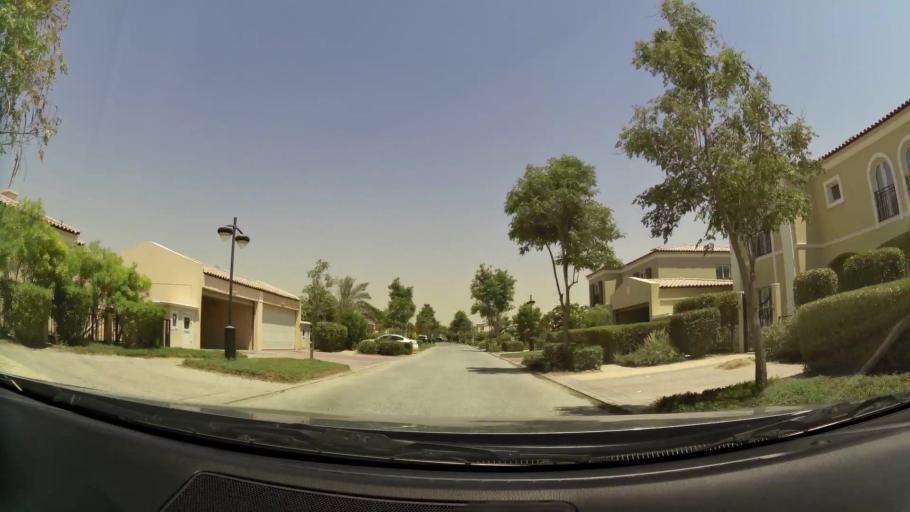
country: AE
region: Dubai
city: Dubai
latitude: 24.9918
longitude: 55.1639
